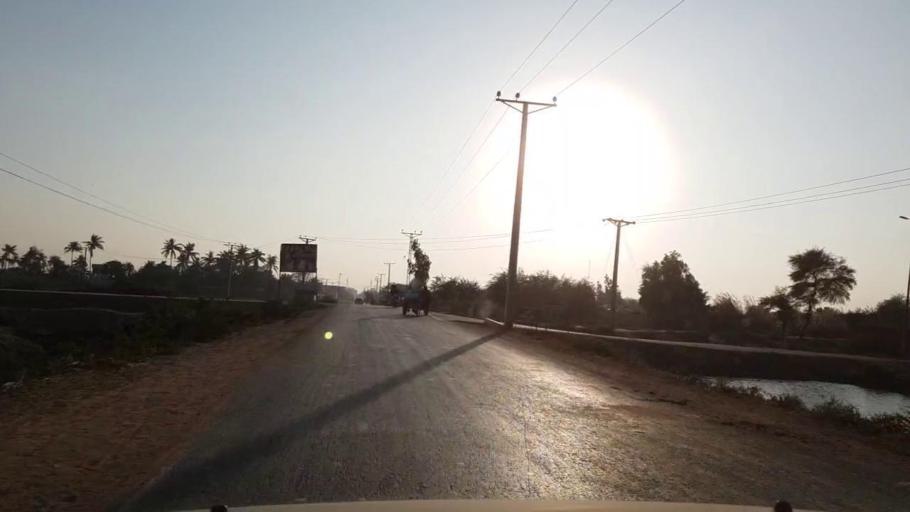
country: PK
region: Sindh
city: Daro Mehar
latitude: 24.6105
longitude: 68.0861
